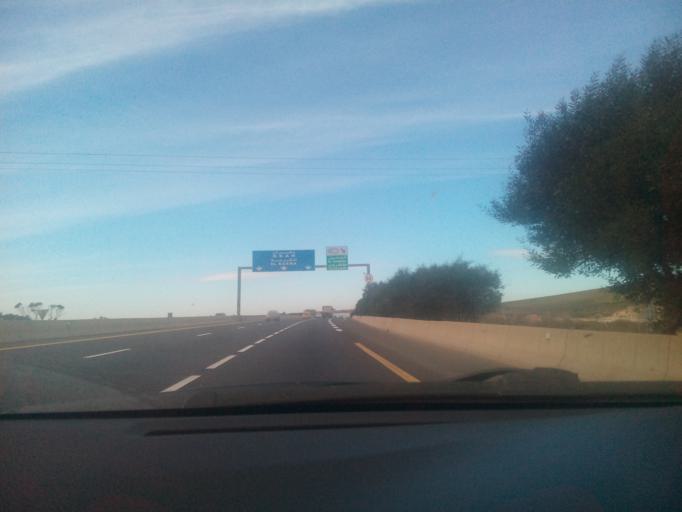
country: DZ
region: Oran
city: Sidi ech Chahmi
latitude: 35.5736
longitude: -0.5508
